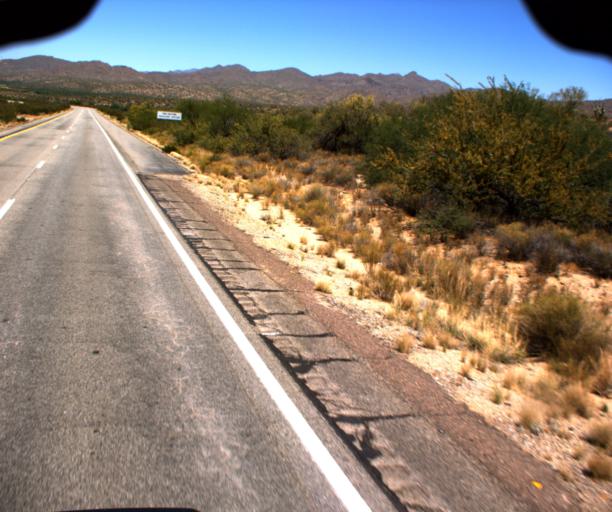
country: US
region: Arizona
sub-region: Yavapai County
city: Bagdad
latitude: 34.3632
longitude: -113.1745
